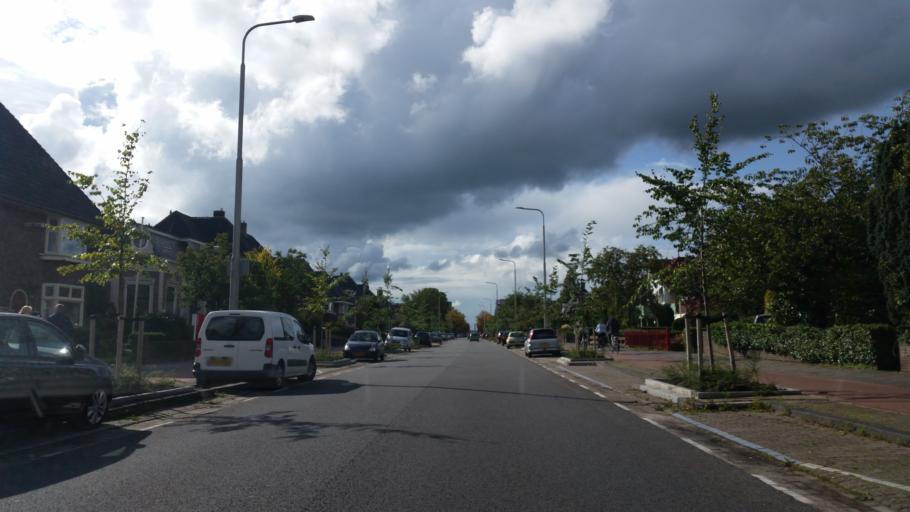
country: NL
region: Friesland
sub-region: Gemeente Leeuwarden
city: Bilgaard
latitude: 53.2041
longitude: 5.7861
